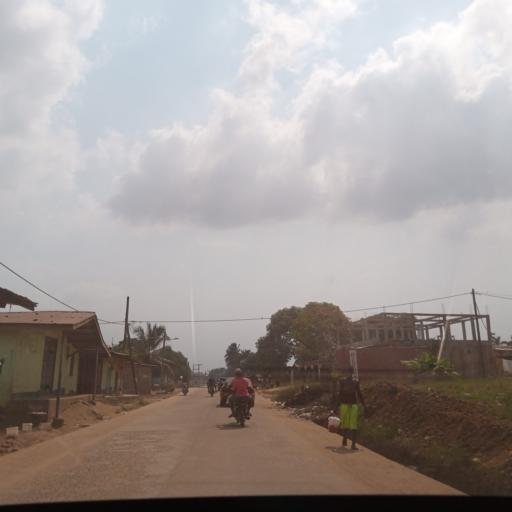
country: LR
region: Montserrado
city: Monrovia
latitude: 6.2874
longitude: -10.6899
